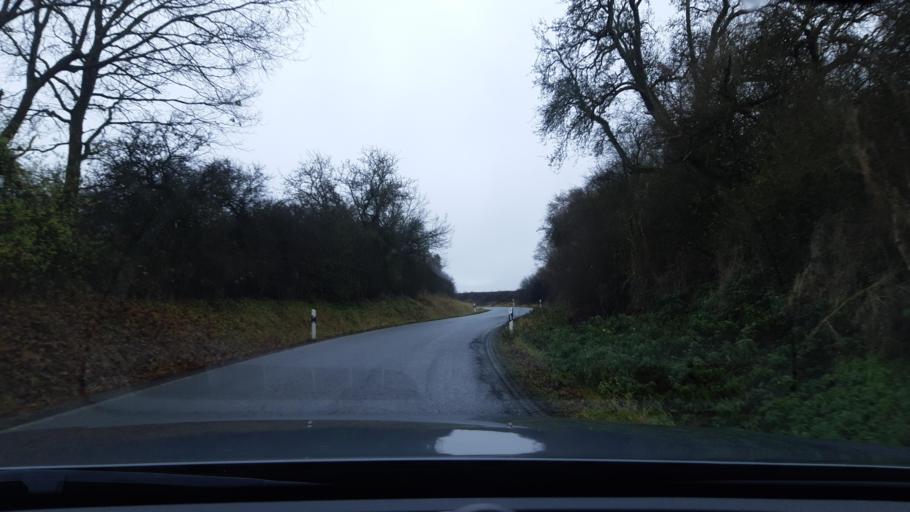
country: DE
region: Hesse
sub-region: Regierungsbezirk Giessen
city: Schoeffengrund
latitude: 50.4990
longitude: 8.5473
